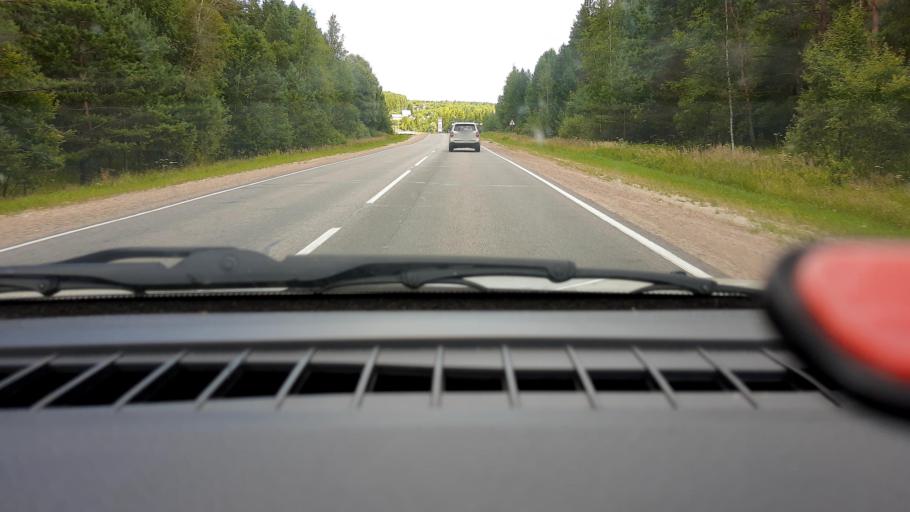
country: RU
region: Nizjnij Novgorod
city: Arzamas
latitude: 55.3816
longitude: 43.9168
